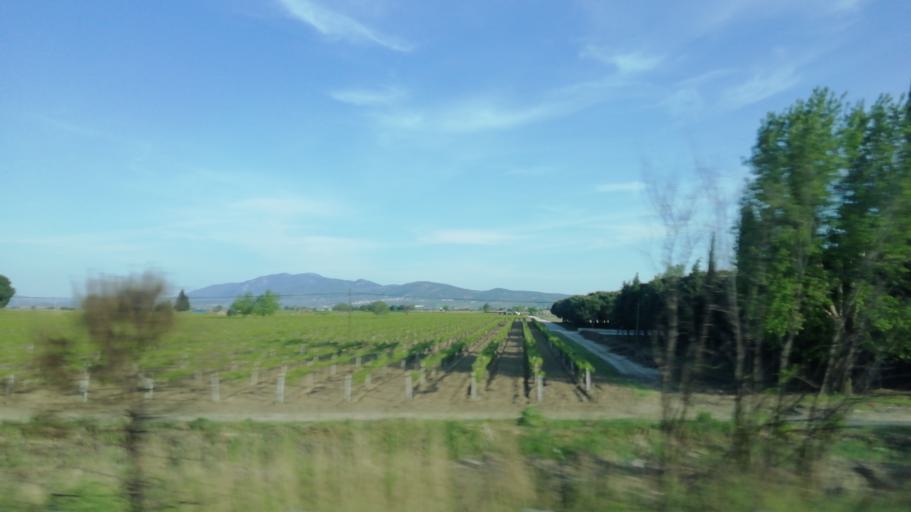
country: TR
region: Manisa
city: Saruhanli
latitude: 38.7476
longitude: 27.6167
